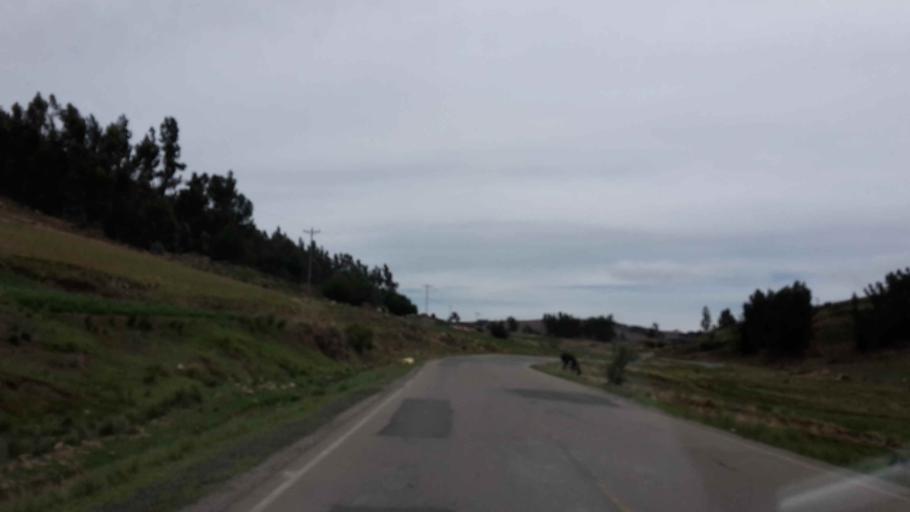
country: BO
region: Cochabamba
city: Arani
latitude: -17.4830
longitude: -65.6044
